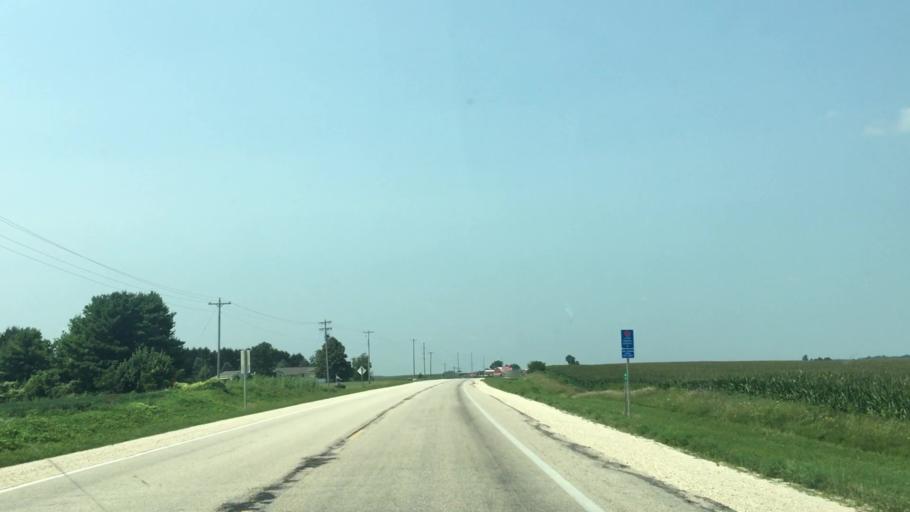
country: US
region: Iowa
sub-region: Fayette County
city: West Union
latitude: 42.9723
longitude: -91.8179
